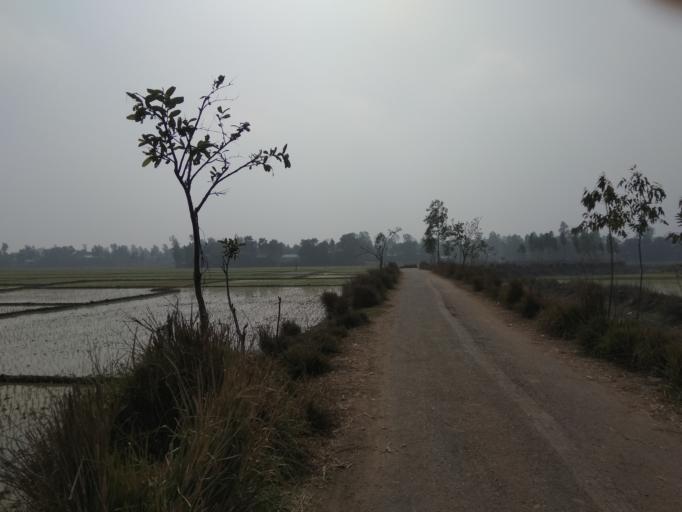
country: BD
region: Rajshahi
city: Bogra
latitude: 24.4692
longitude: 89.2679
